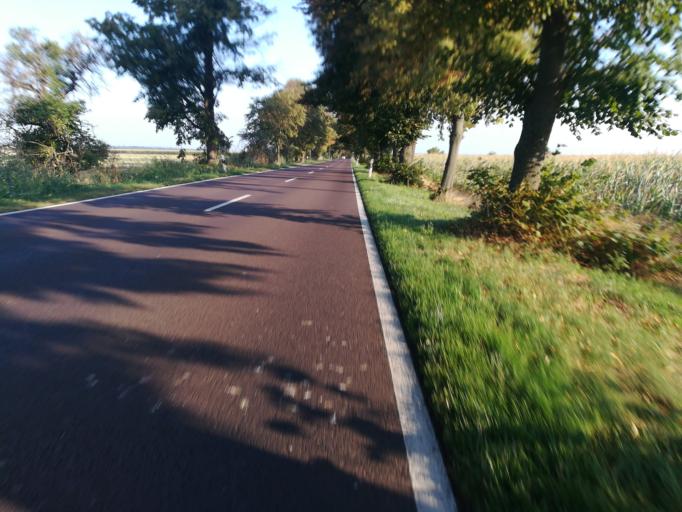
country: DE
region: Saxony-Anhalt
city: Haldensleben I
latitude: 52.2450
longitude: 11.4370
